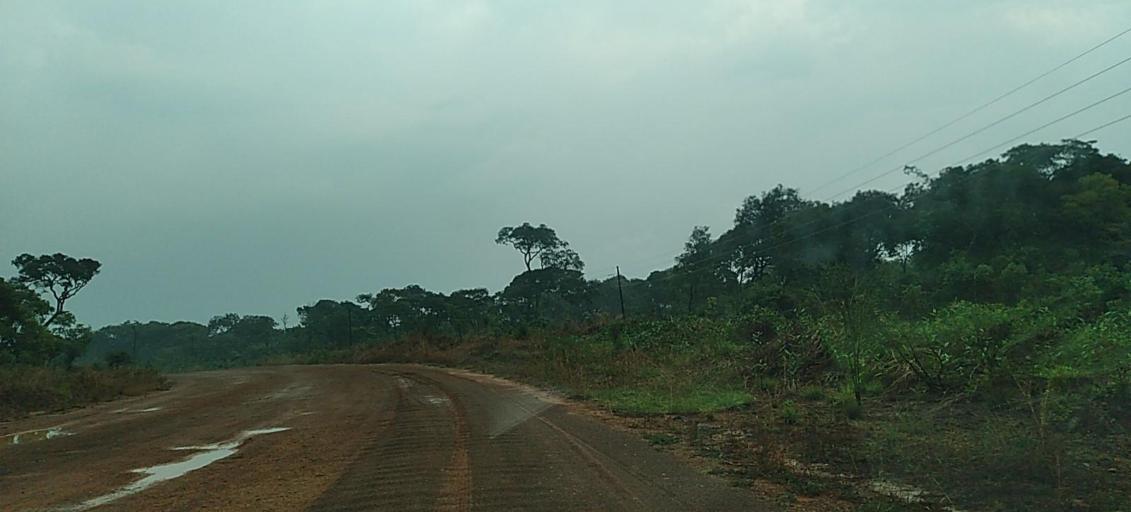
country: ZM
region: North-Western
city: Mwinilunga
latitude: -11.5883
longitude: 24.3869
